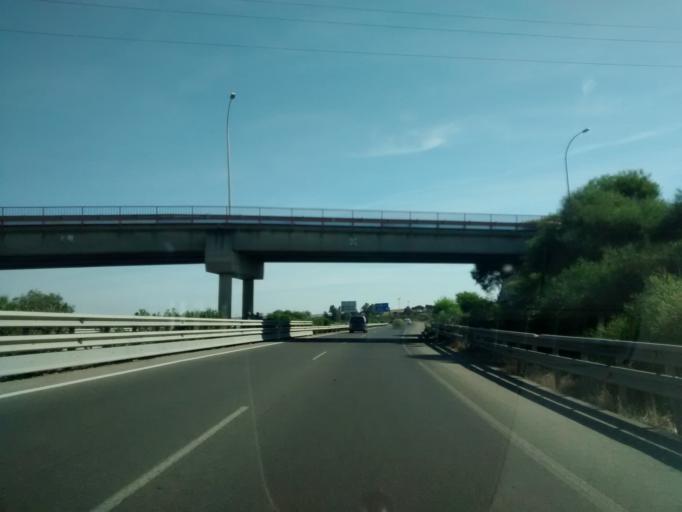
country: ES
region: Andalusia
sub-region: Provincia de Cadiz
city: Chiclana de la Frontera
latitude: 36.4059
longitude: -6.1238
